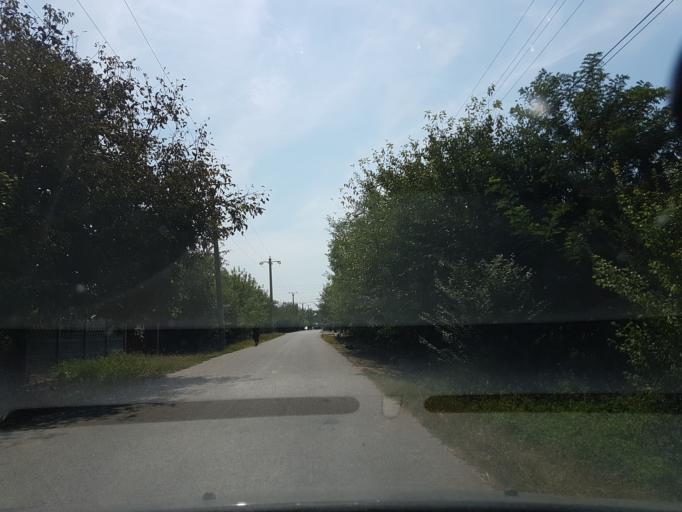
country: RO
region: Giurgiu
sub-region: Comuna Herasti
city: Herasti
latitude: 44.2134
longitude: 26.3598
